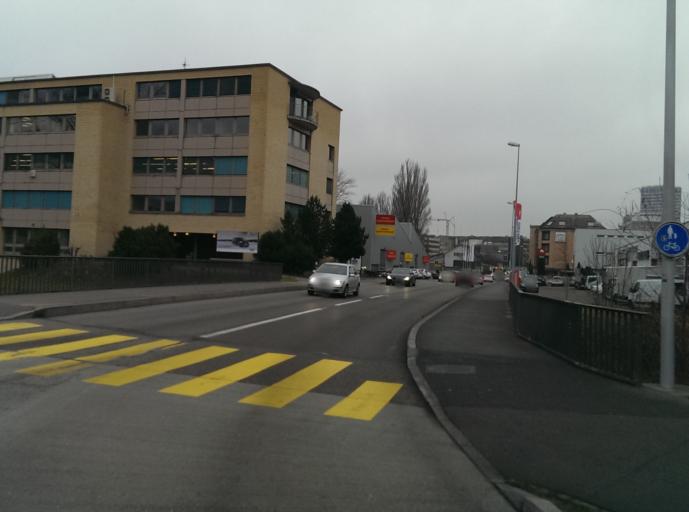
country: CH
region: Zurich
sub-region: Bezirk Dietikon
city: Dietikon / Vorstadt
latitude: 47.4137
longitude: 8.4005
